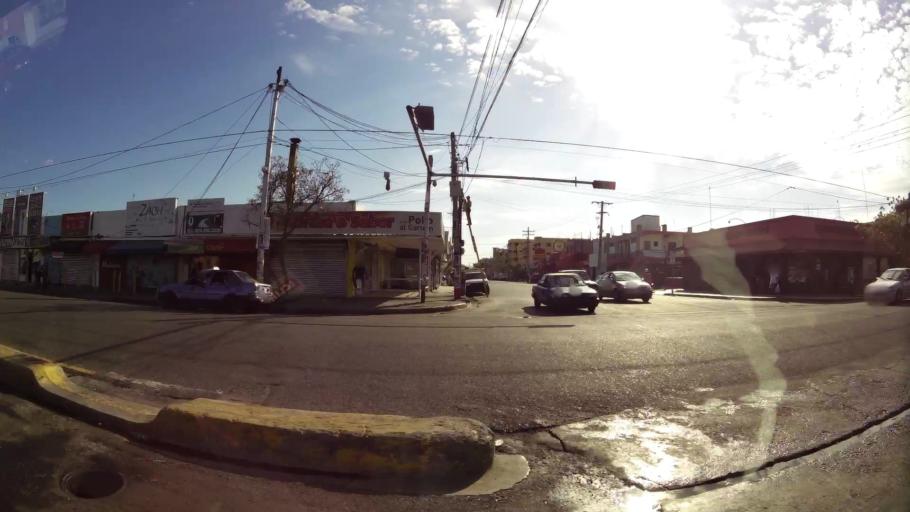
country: DO
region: Santo Domingo
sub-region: Santo Domingo
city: Santo Domingo Este
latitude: 18.4949
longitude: -69.8514
